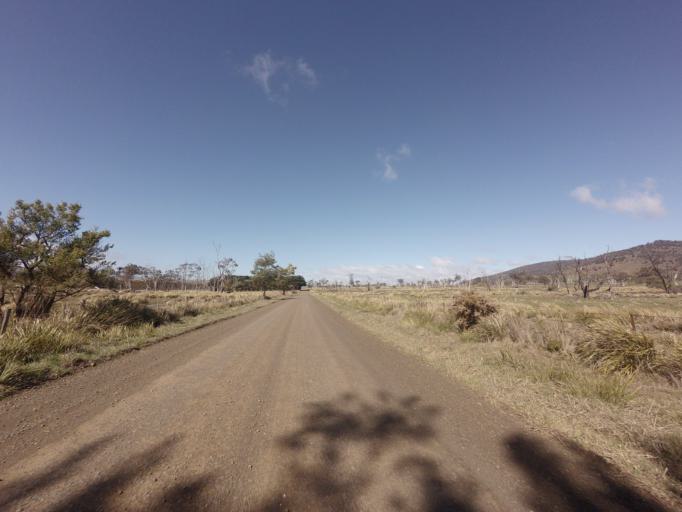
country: AU
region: Tasmania
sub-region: Northern Midlands
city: Evandale
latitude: -41.9418
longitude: 147.4267
